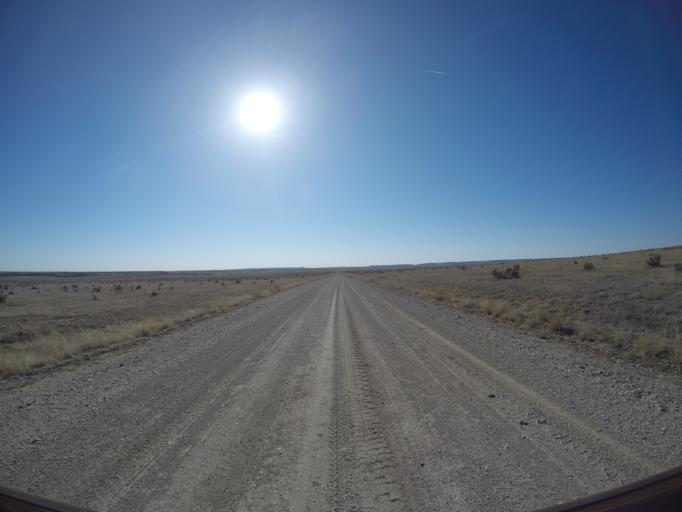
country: US
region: Colorado
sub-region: Otero County
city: La Junta
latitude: 37.7306
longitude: -103.6206
